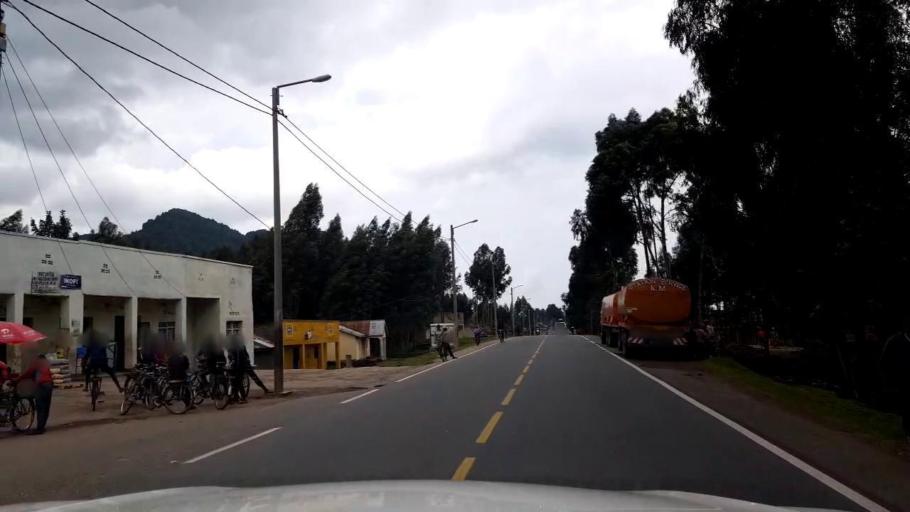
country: RW
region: Western Province
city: Gisenyi
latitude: -1.6366
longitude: 29.4054
